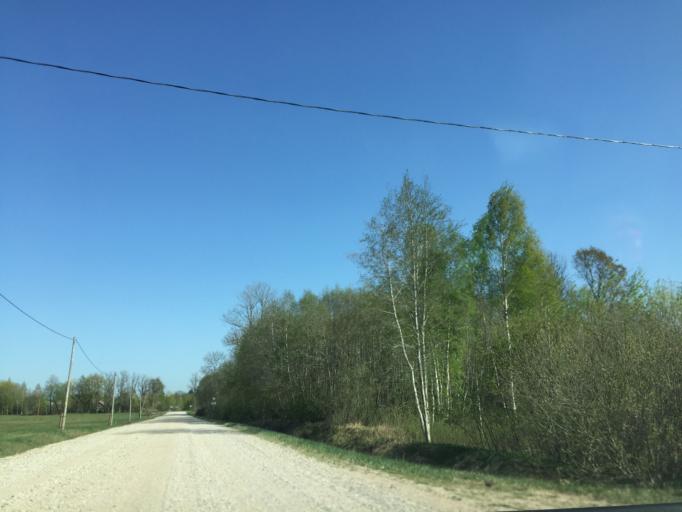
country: LV
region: Skriveri
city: Skriveri
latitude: 56.8344
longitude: 25.1259
